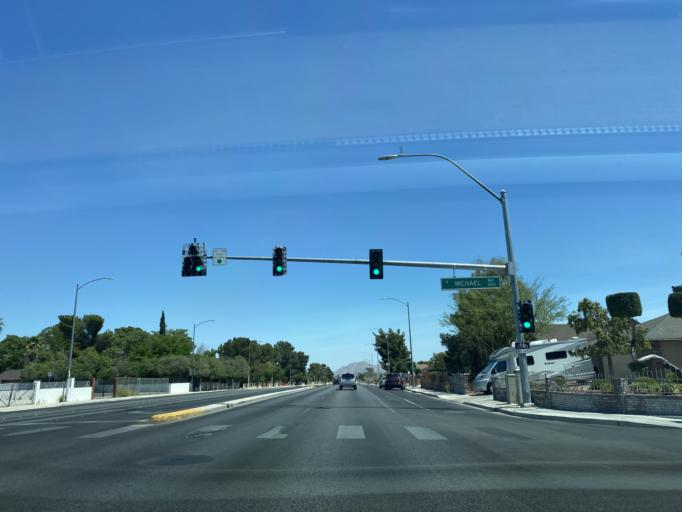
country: US
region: Nevada
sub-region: Clark County
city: Las Vegas
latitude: 36.1955
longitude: -115.2151
